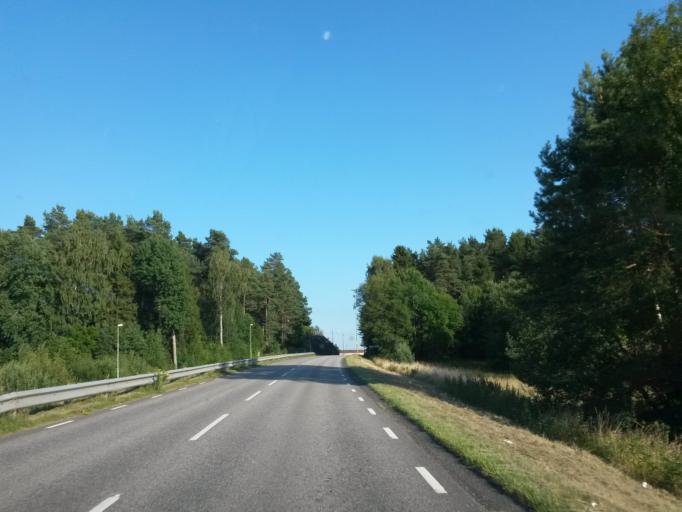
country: SE
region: Vaestra Goetaland
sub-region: Vargarda Kommun
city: Vargarda
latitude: 58.0396
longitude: 12.8053
